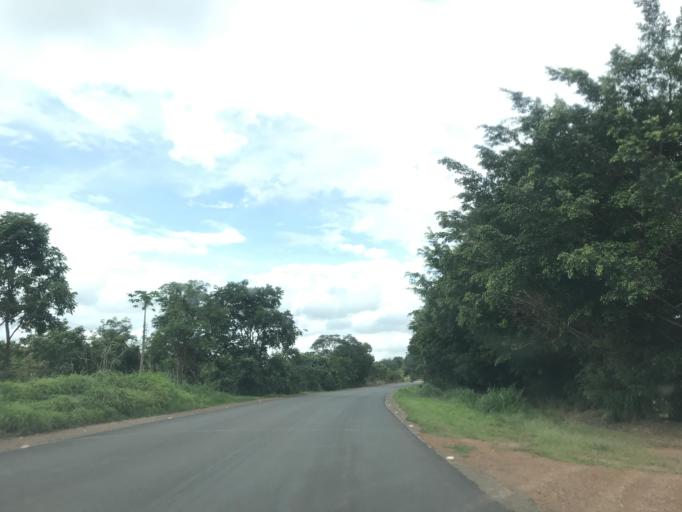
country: BR
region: Goias
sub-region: Bela Vista De Goias
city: Bela Vista de Goias
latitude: -17.0386
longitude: -48.6624
